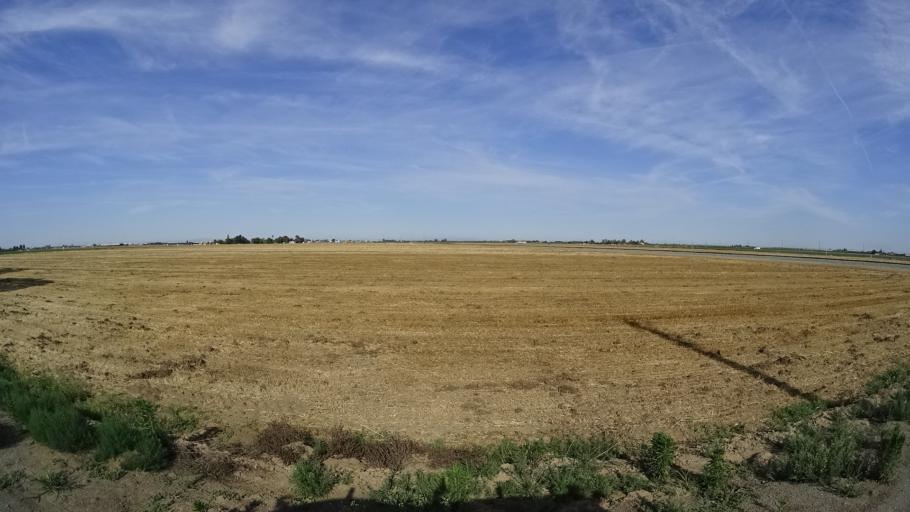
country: US
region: California
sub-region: Kings County
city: Home Garden
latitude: 36.3383
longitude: -119.5559
